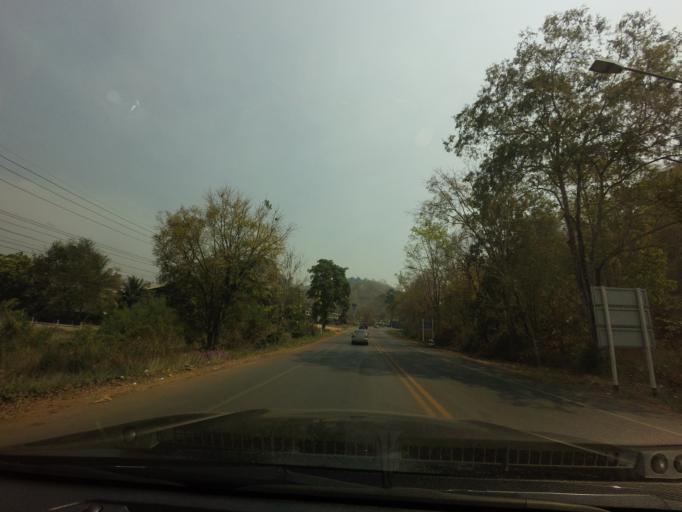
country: TH
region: Kanchanaburi
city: Thong Pha Phum
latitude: 14.7381
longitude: 98.6414
